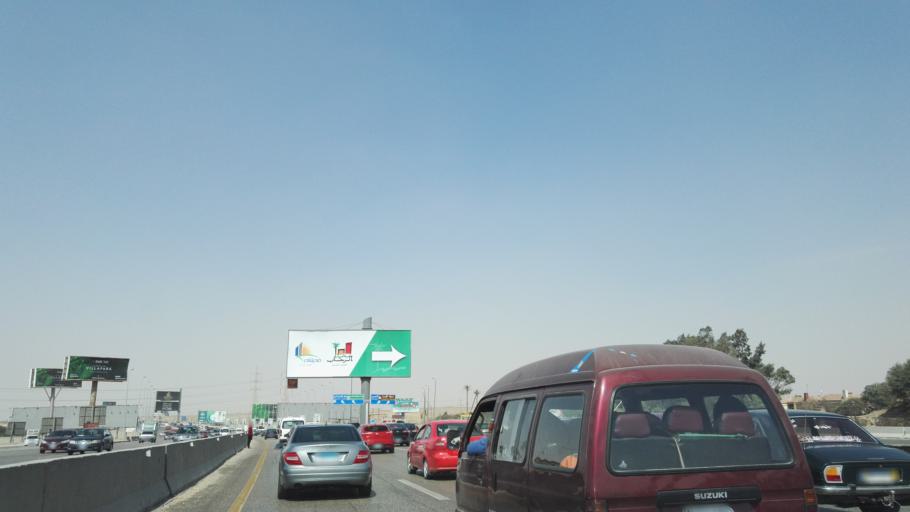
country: EG
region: Muhafazat al Qalyubiyah
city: Al Khankah
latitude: 30.0738
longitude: 31.4317
